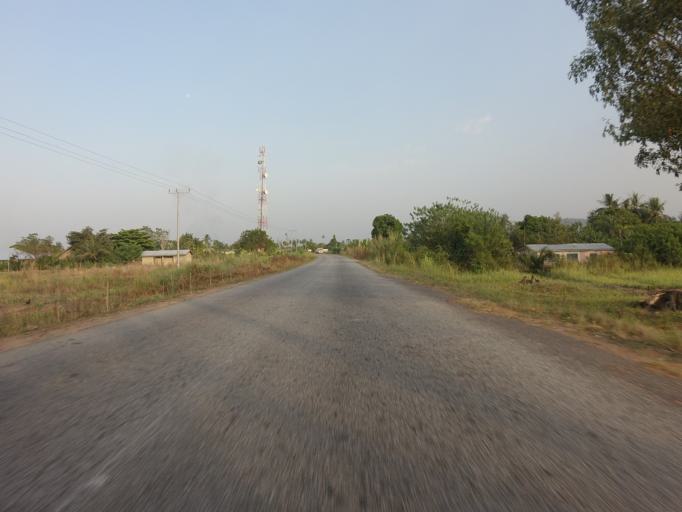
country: GH
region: Volta
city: Ho
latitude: 6.5729
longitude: 0.3622
